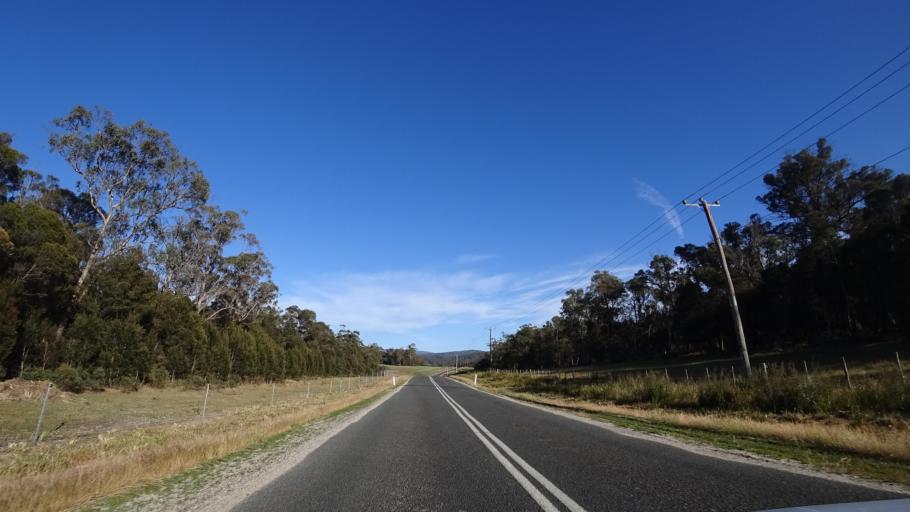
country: AU
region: Tasmania
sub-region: Break O'Day
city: St Helens
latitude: -41.2816
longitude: 148.1282
